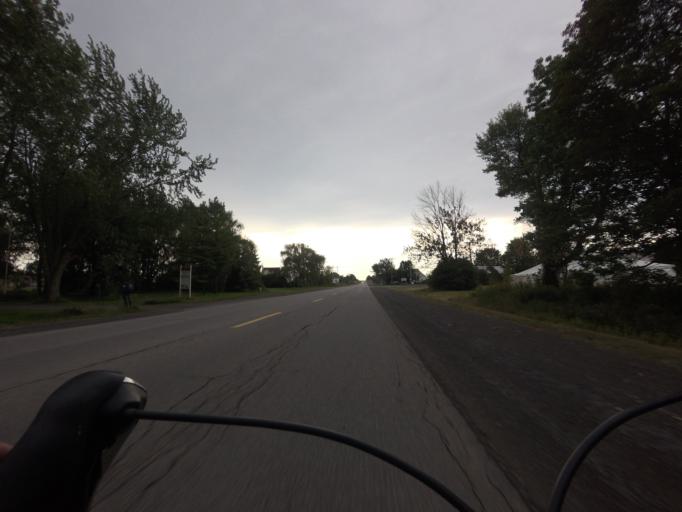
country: CA
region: Ontario
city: Bells Corners
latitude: 45.1751
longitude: -75.7170
